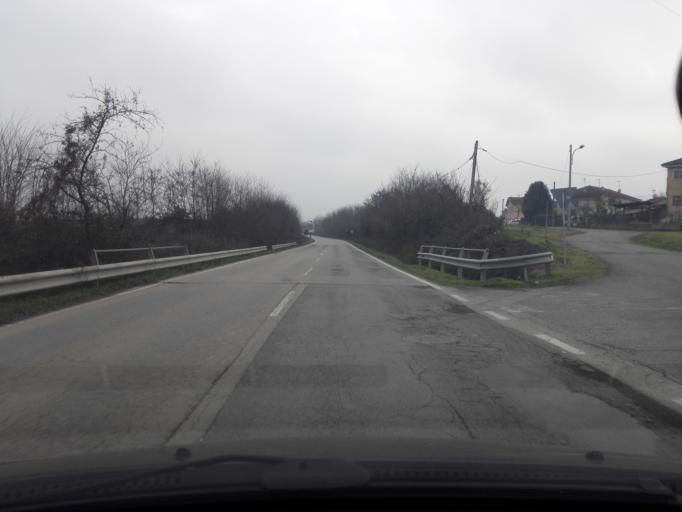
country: IT
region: Piedmont
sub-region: Provincia di Alessandria
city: Bosco Marengo
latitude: 44.8168
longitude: 8.6873
